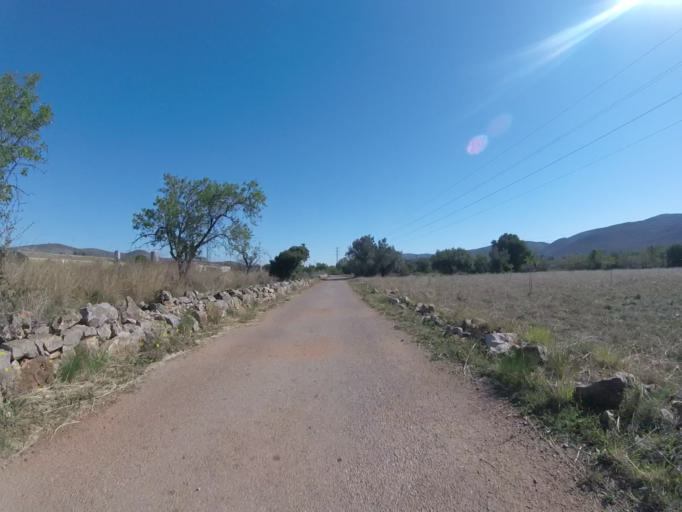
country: ES
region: Valencia
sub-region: Provincia de Castello
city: Santa Magdalena de Pulpis
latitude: 40.3517
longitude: 0.2802
